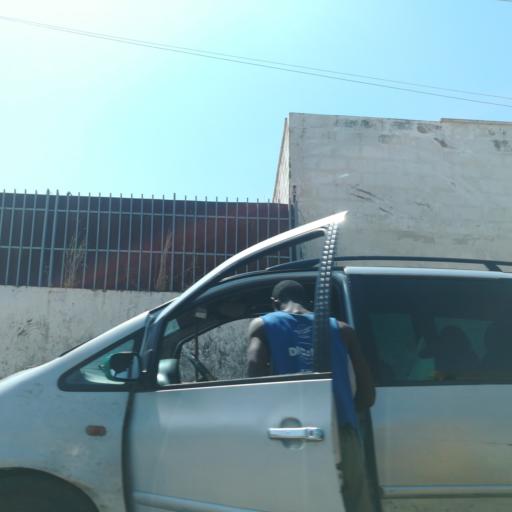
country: NG
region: Kano
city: Kano
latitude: 12.0076
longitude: 8.5416
